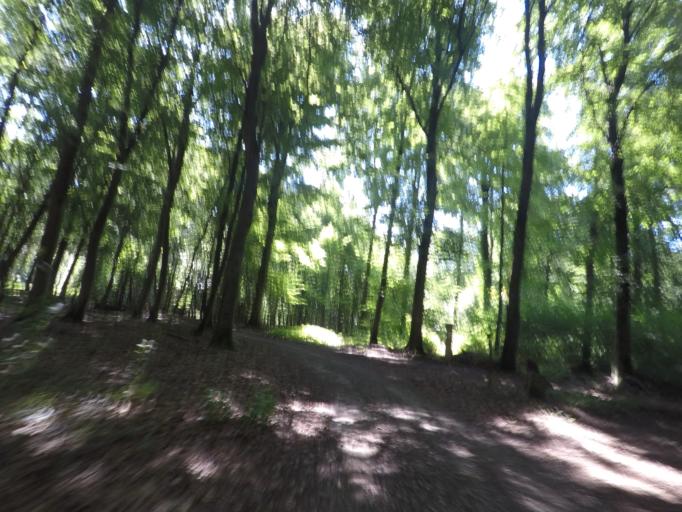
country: LU
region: Luxembourg
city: Bridel
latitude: 49.6412
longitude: 6.0766
